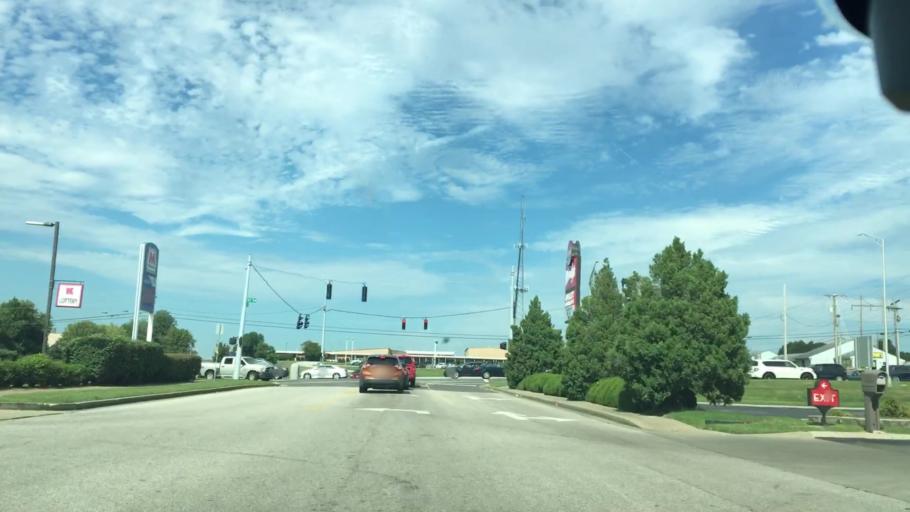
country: US
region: Kentucky
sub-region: Daviess County
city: Owensboro
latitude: 37.7556
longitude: -87.0675
